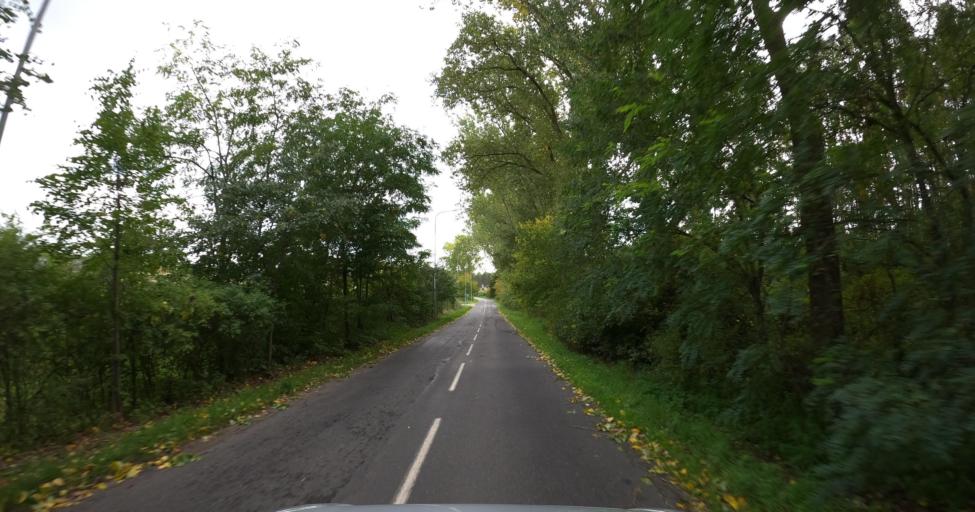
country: PL
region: Lubusz
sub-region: Powiat zielonogorski
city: Zabor
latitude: 51.9467
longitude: 15.6498
